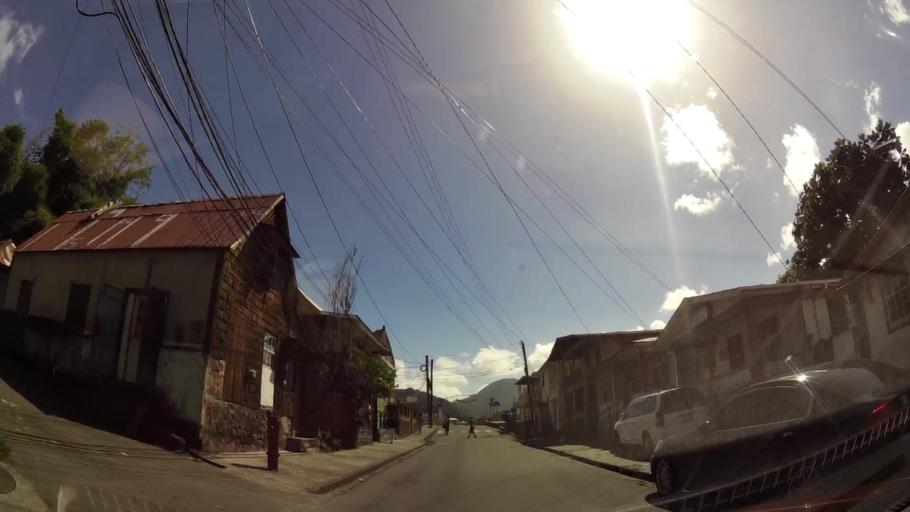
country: DM
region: Saint George
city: Roseau
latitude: 15.3018
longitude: -61.3889
